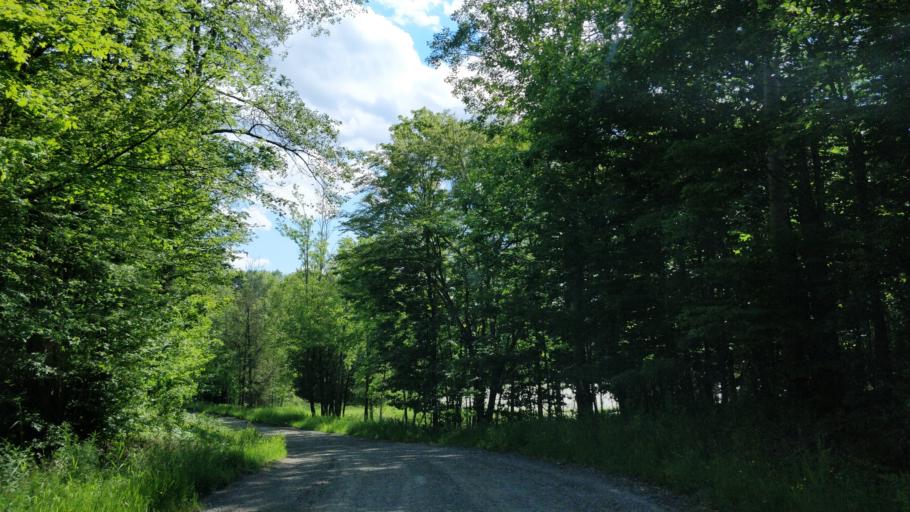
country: CA
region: Ontario
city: Perth
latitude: 44.6863
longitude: -76.5335
